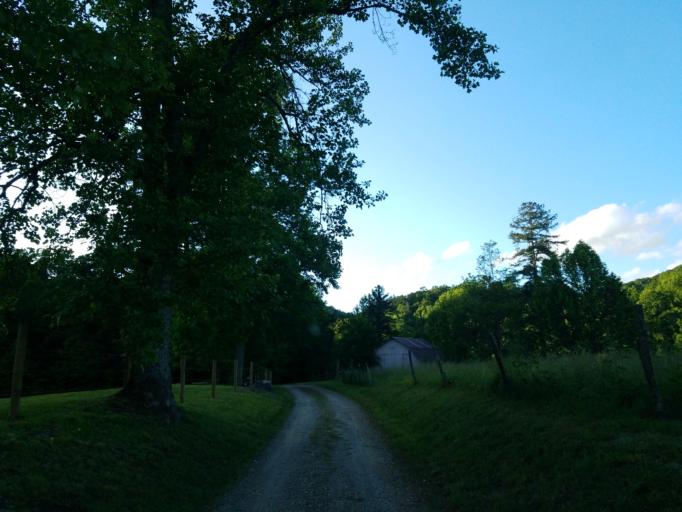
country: US
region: Georgia
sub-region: Union County
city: Blairsville
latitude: 34.7129
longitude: -84.0257
